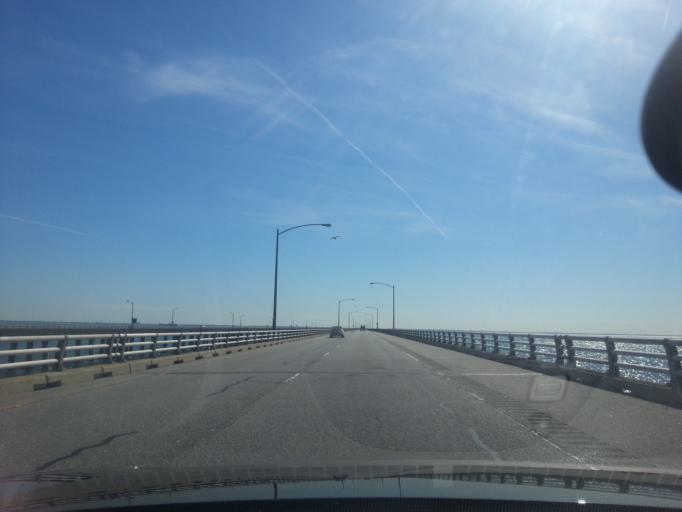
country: US
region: Virginia
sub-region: City of Virginia Beach
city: Virginia Beach
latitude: 37.0263
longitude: -76.0888
